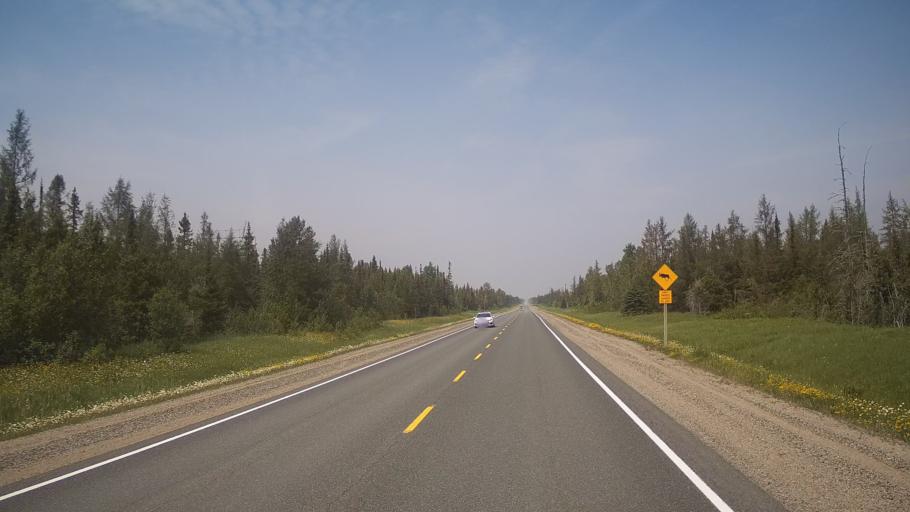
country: CA
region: Ontario
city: Timmins
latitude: 48.7832
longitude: -81.3647
